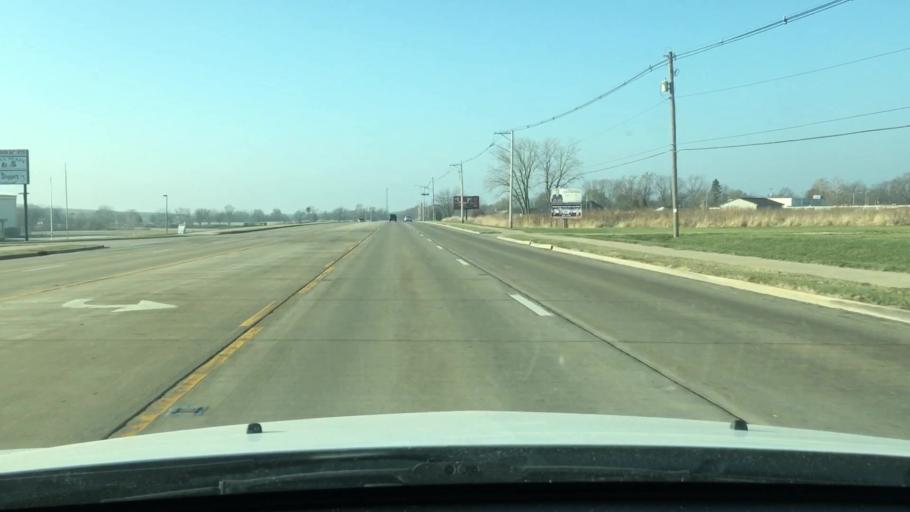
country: US
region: Illinois
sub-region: Tazewell County
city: East Peoria
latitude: 40.6890
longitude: -89.5039
